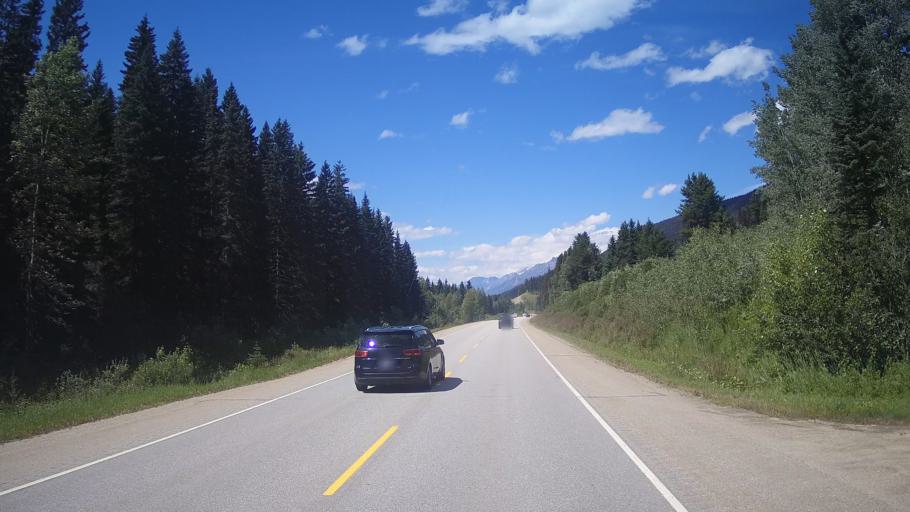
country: CA
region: Alberta
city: Jasper Park Lodge
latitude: 52.8734
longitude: -118.6869
